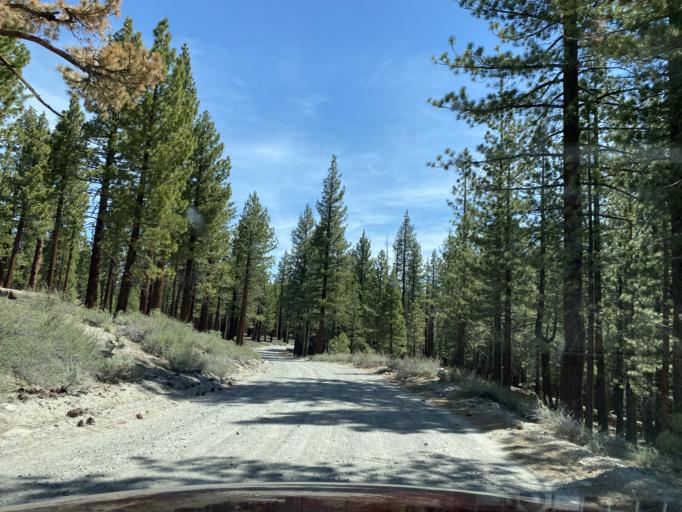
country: US
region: California
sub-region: Mono County
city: Mammoth Lakes
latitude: 37.7684
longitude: -119.0224
